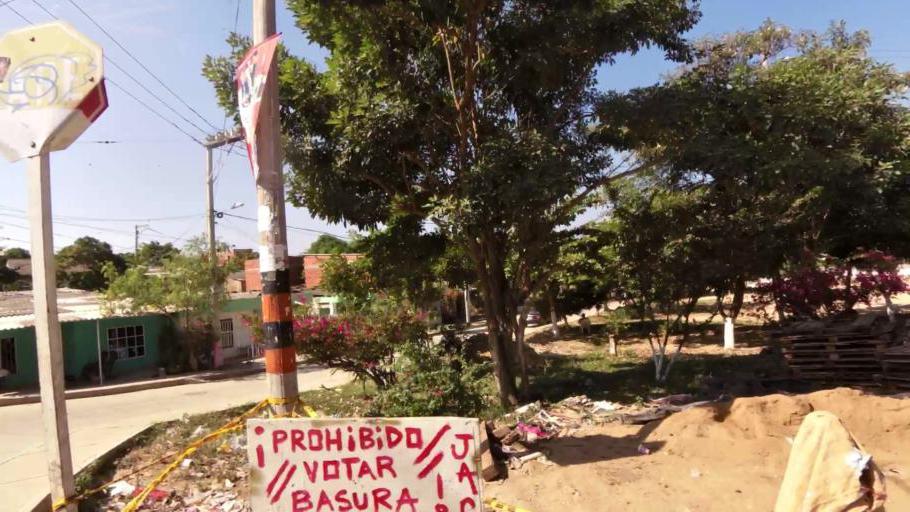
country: CO
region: Bolivar
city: Cartagena
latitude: 10.3731
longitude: -75.4959
